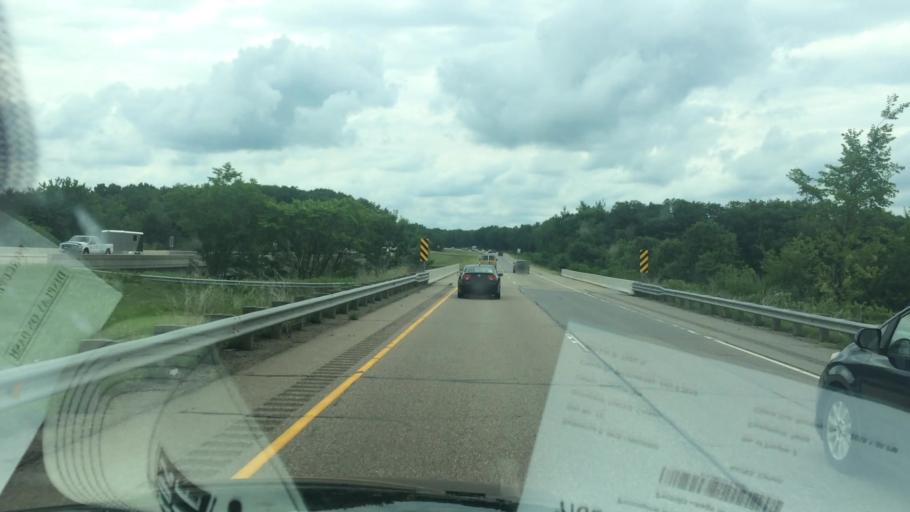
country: US
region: Wisconsin
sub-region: Marathon County
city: Mosinee
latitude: 44.6832
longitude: -89.6411
